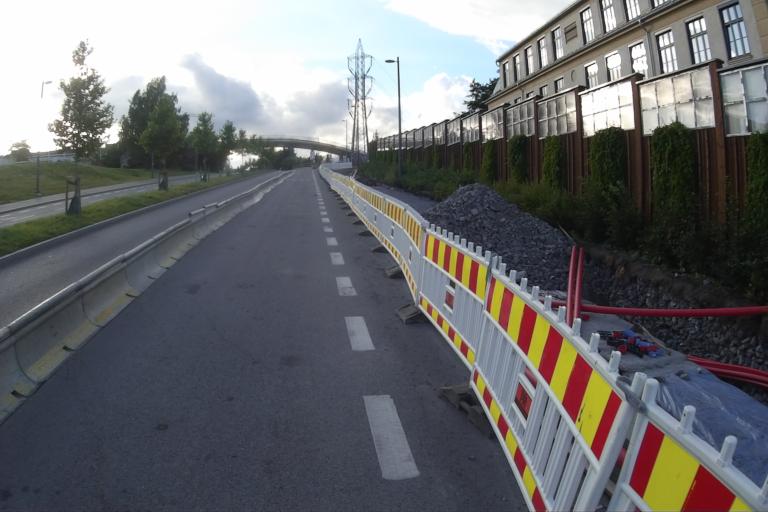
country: NO
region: Oslo
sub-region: Oslo
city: Oslo
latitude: 59.9312
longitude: 10.8016
